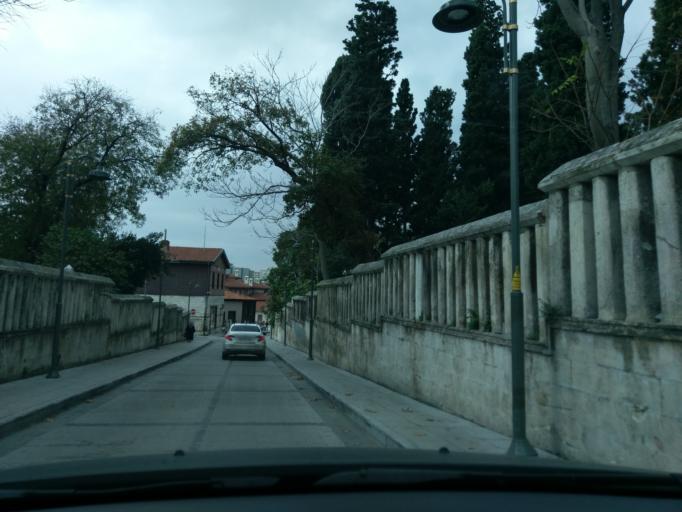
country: TR
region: Istanbul
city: Zeytinburnu
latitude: 41.0142
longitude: 28.9212
